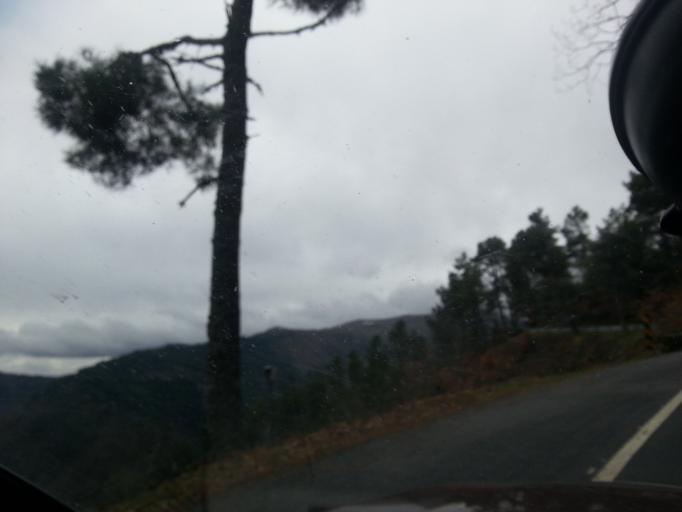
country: PT
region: Guarda
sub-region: Manteigas
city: Manteigas
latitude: 40.4136
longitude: -7.5378
